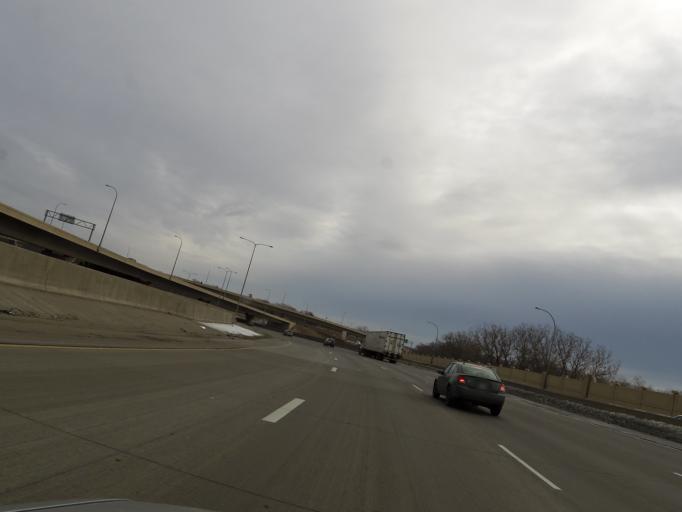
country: US
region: Minnesota
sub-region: Hennepin County
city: Richfield
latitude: 44.8900
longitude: -93.2789
